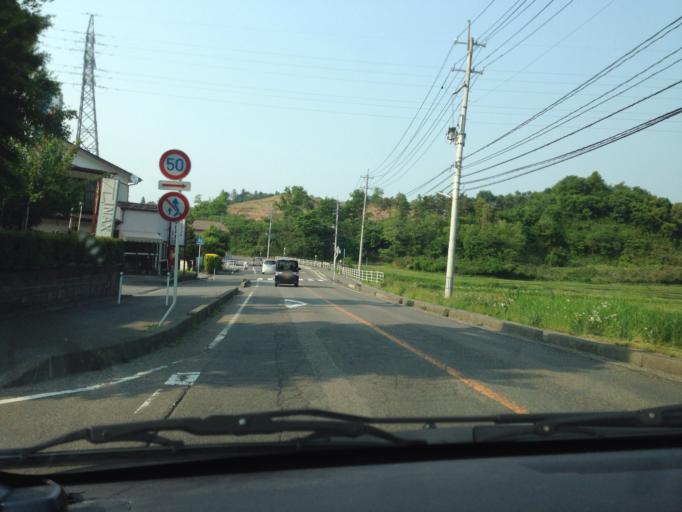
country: JP
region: Tochigi
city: Kuroiso
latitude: 37.1017
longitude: 140.1971
